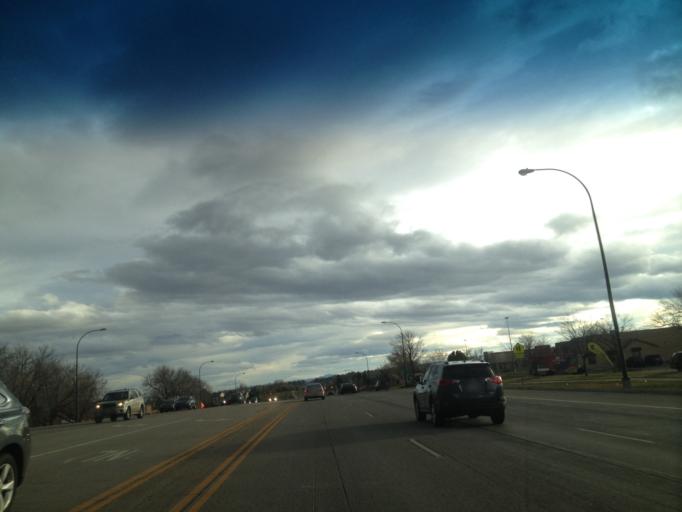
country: US
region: Colorado
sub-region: Adams County
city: Westminster
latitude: 39.8592
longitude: -105.0817
